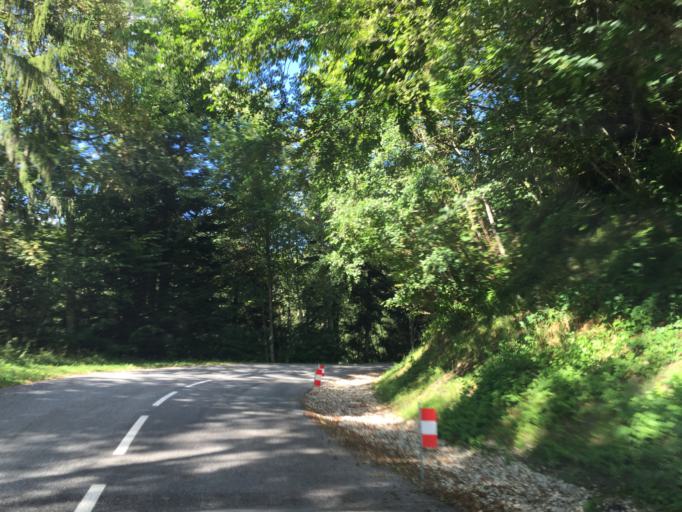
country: FR
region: Rhone-Alpes
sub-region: Departement de la Savoie
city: Coise-Saint-Jean-Pied-Gauthier
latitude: 45.4749
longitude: 6.1874
